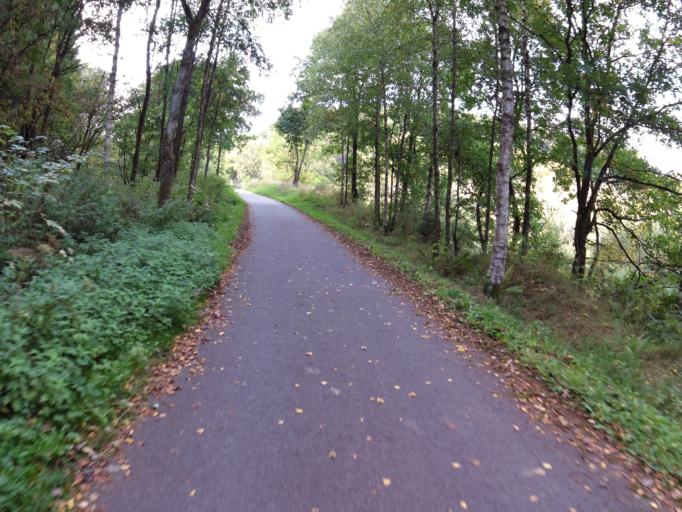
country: BE
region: Wallonia
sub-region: Province de Liege
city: Saint-Vith
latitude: 50.2452
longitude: 6.1528
